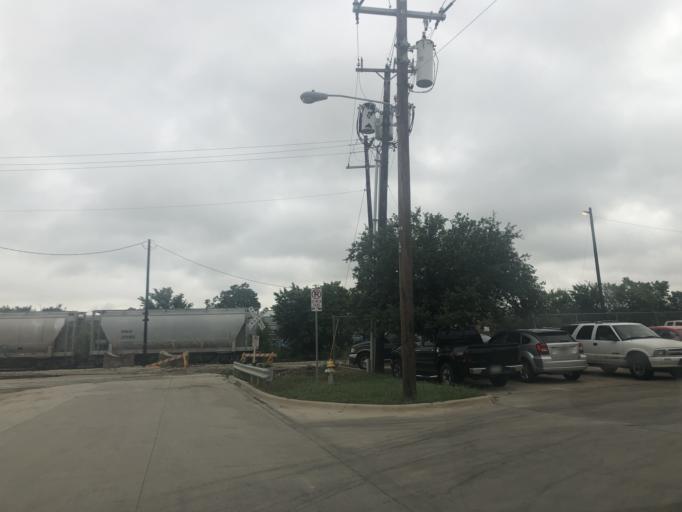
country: US
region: Texas
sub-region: Dallas County
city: Cockrell Hill
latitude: 32.7745
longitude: -96.8585
